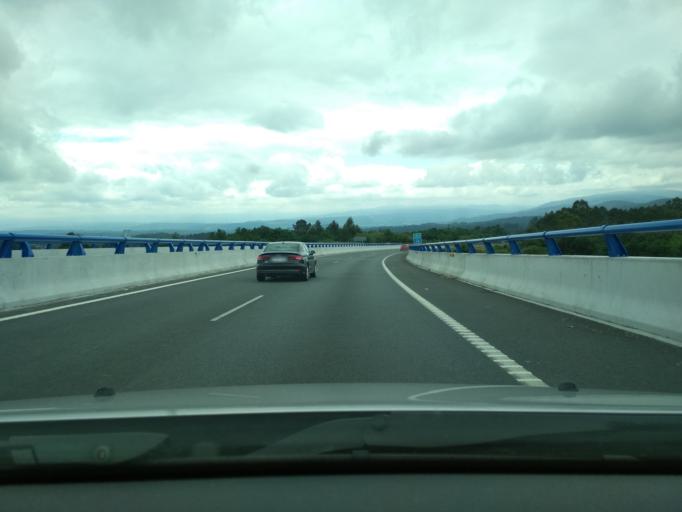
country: ES
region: Galicia
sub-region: Provincia da Coruna
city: Santiago de Compostela
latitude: 42.8321
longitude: -8.5722
